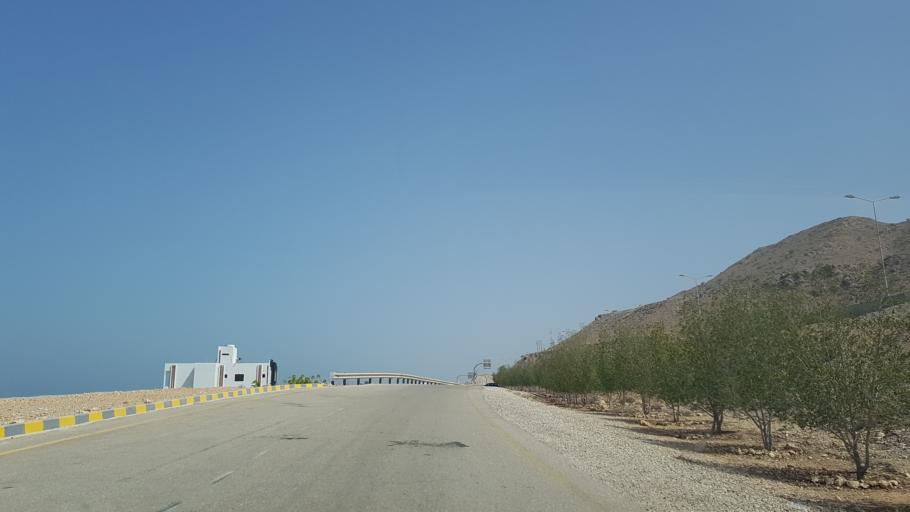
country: OM
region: Ash Sharqiyah
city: Sur
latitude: 22.8447
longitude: 59.2412
